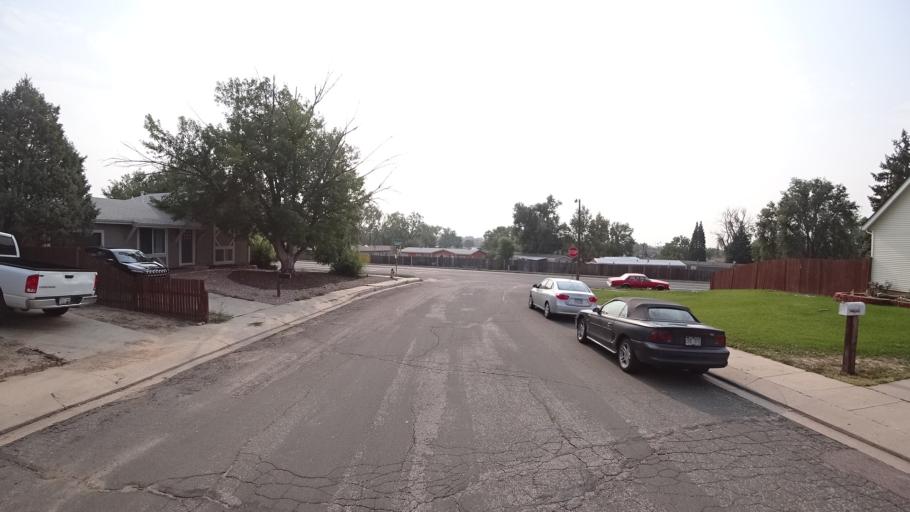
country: US
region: Colorado
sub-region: El Paso County
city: Stratmoor
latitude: 38.8002
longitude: -104.7642
